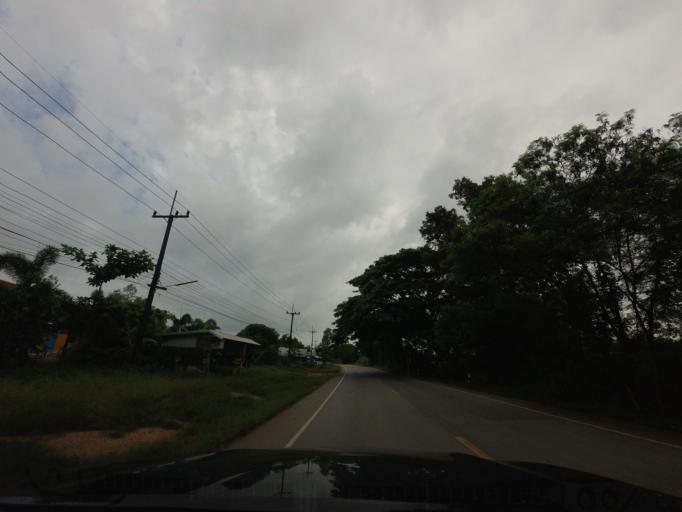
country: TH
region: Changwat Udon Thani
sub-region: Amphoe Ban Phue
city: Ban Phue
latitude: 17.7229
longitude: 102.3938
